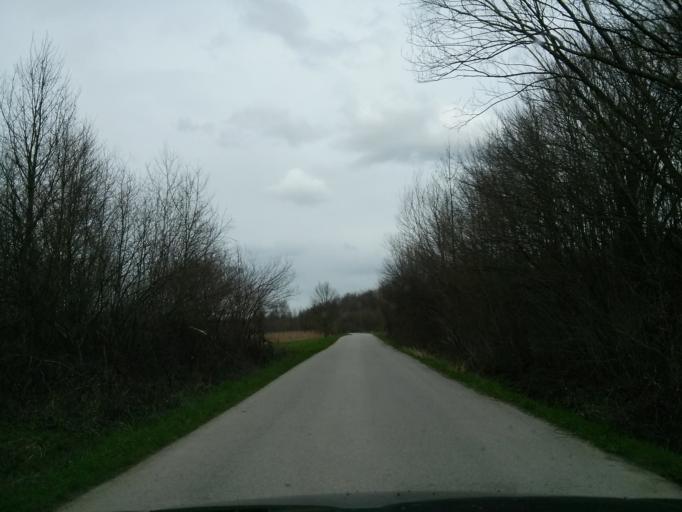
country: HR
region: Sisacko-Moslavacka
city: Glina
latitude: 45.2910
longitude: 15.9916
